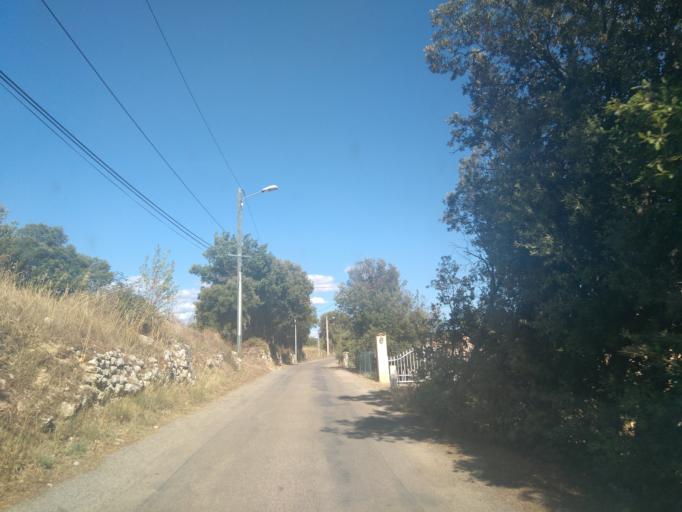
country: FR
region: Provence-Alpes-Cote d'Azur
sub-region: Departement du Var
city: Regusse
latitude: 43.7025
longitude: 6.0974
